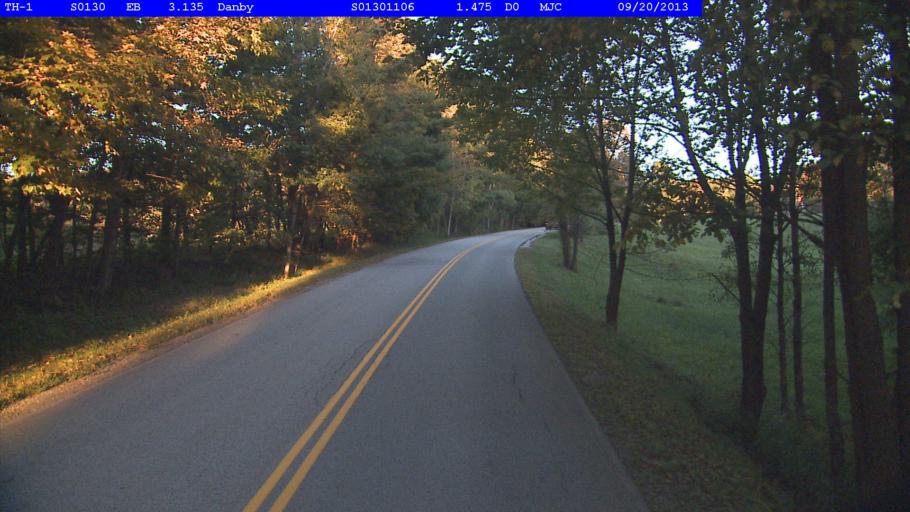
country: US
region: New York
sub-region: Washington County
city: Granville
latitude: 43.3667
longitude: -73.0966
